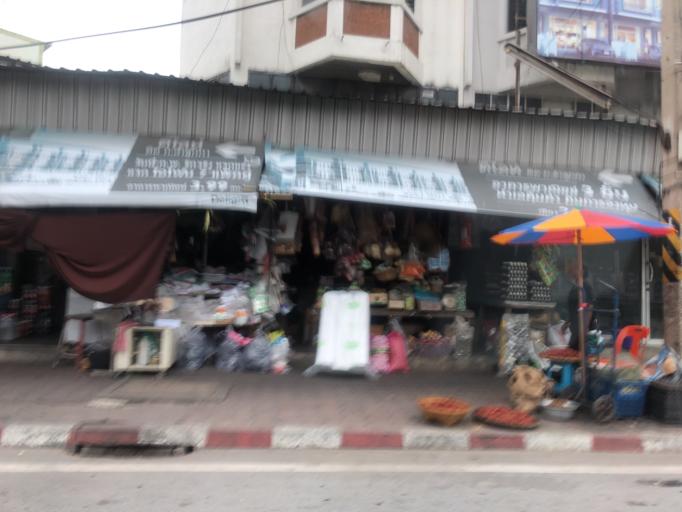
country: TH
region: Bangkok
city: Sai Mai
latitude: 13.9501
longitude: 100.6228
